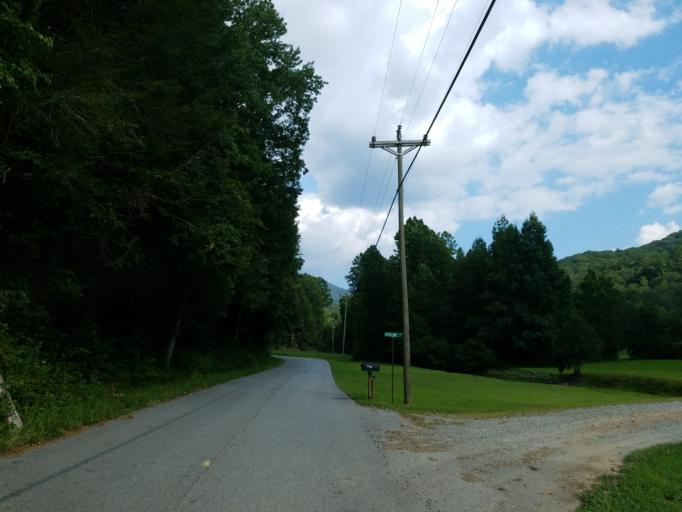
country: US
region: Georgia
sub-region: Fannin County
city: Blue Ridge
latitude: 34.7768
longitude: -84.3804
